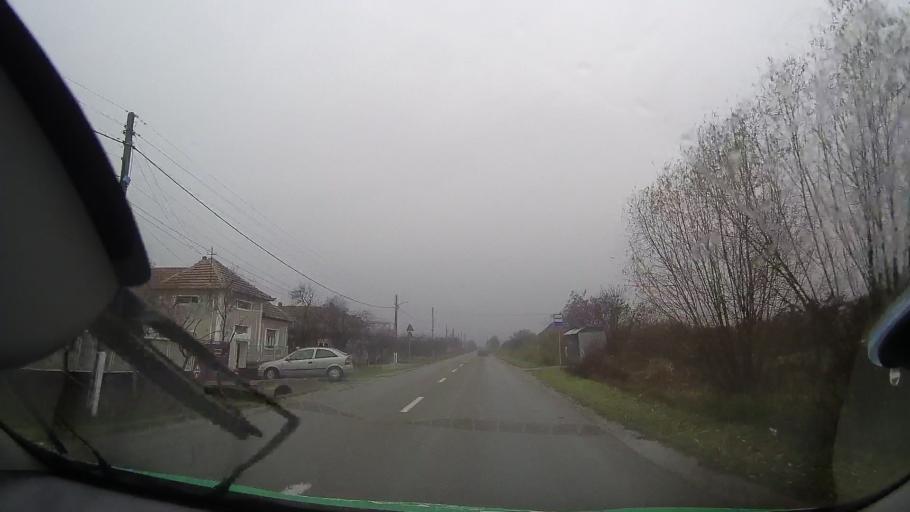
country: RO
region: Bihor
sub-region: Comuna Tulca
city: Tulca
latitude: 46.7937
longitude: 21.7456
